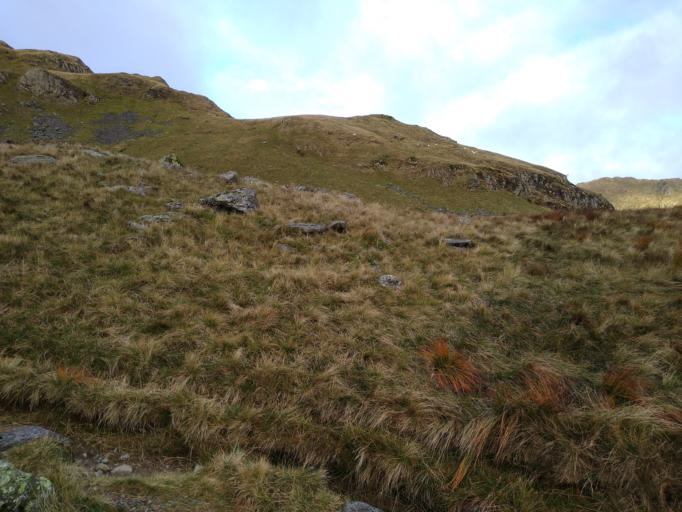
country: GB
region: England
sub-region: Cumbria
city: Windermere
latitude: 54.4836
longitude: -2.8408
